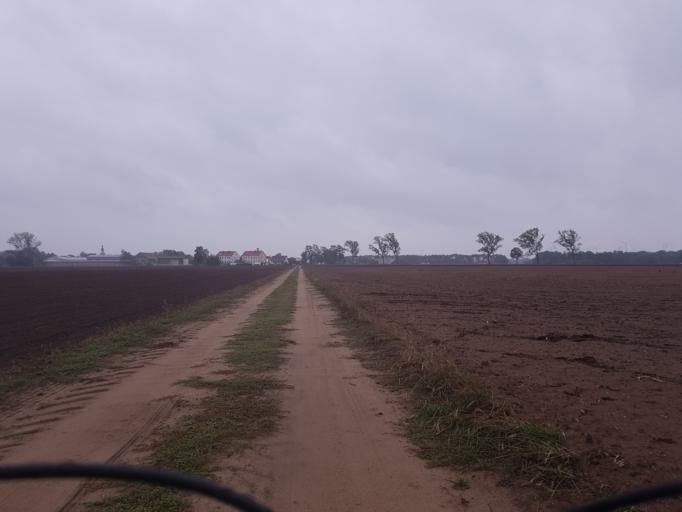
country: DE
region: Brandenburg
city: Schilda
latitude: 51.5583
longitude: 13.3579
